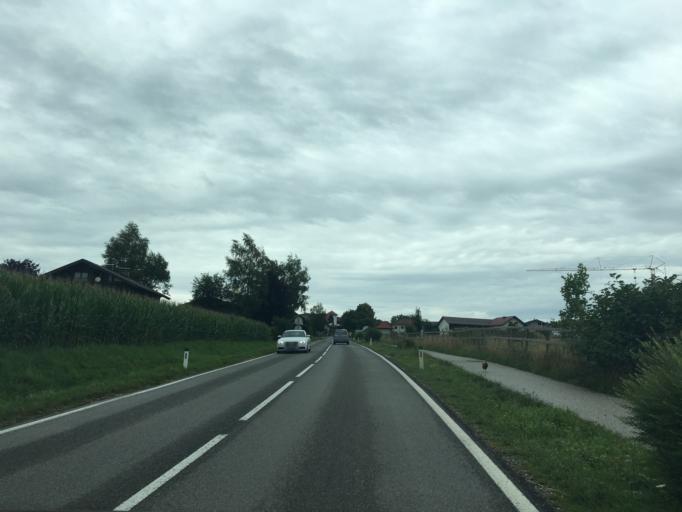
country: AT
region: Salzburg
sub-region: Politischer Bezirk Salzburg-Umgebung
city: Dorfbeuern
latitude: 48.0408
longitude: 12.9884
